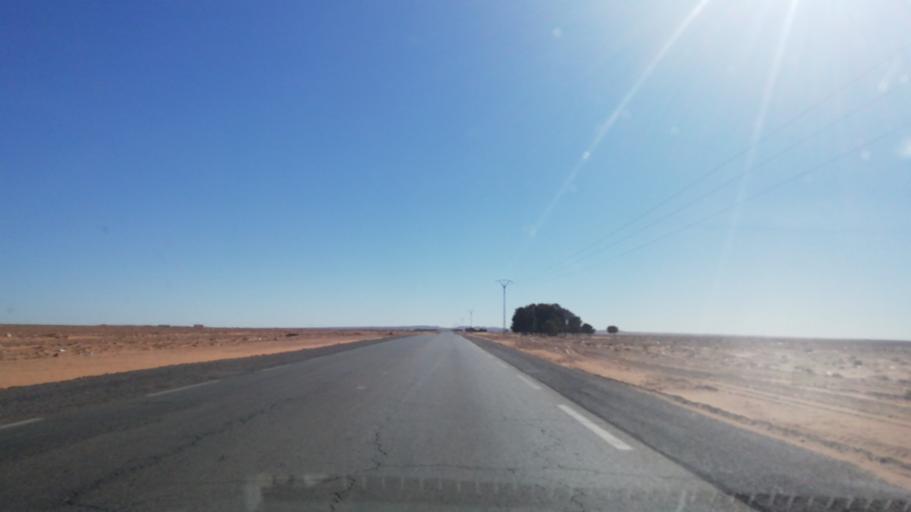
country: DZ
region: Saida
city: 'Ain el Hadjar
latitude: 34.0081
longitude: 0.1212
